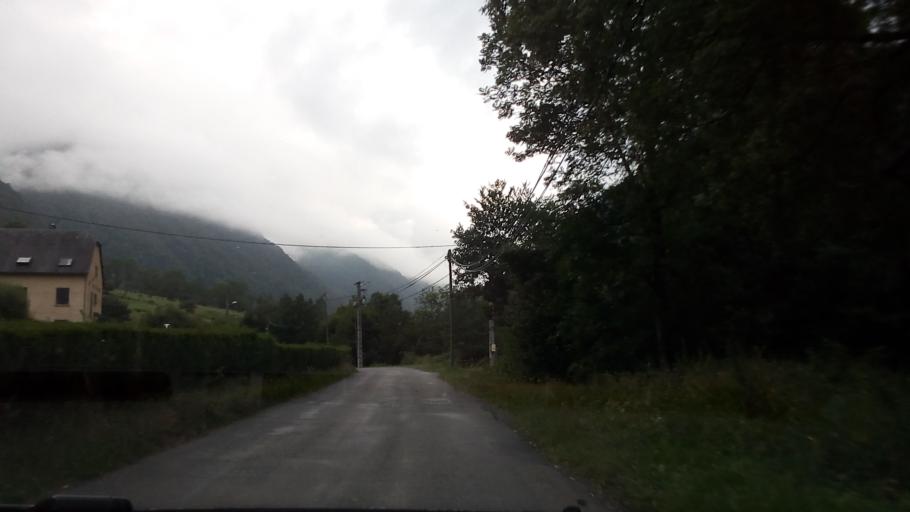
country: FR
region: Midi-Pyrenees
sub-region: Departement des Hautes-Pyrenees
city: Cauterets
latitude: 42.9304
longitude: -0.1802
